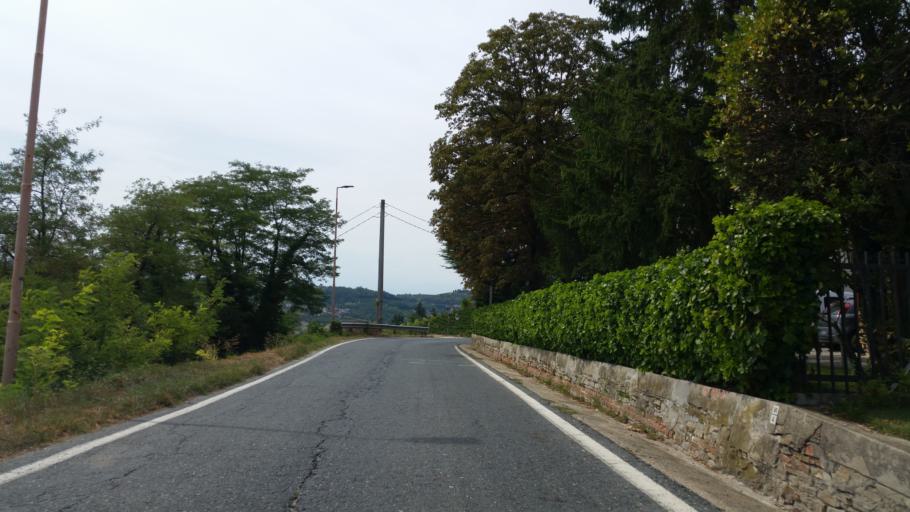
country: IT
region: Piedmont
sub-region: Provincia di Cuneo
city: Ricca
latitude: 44.6663
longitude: 8.0622
